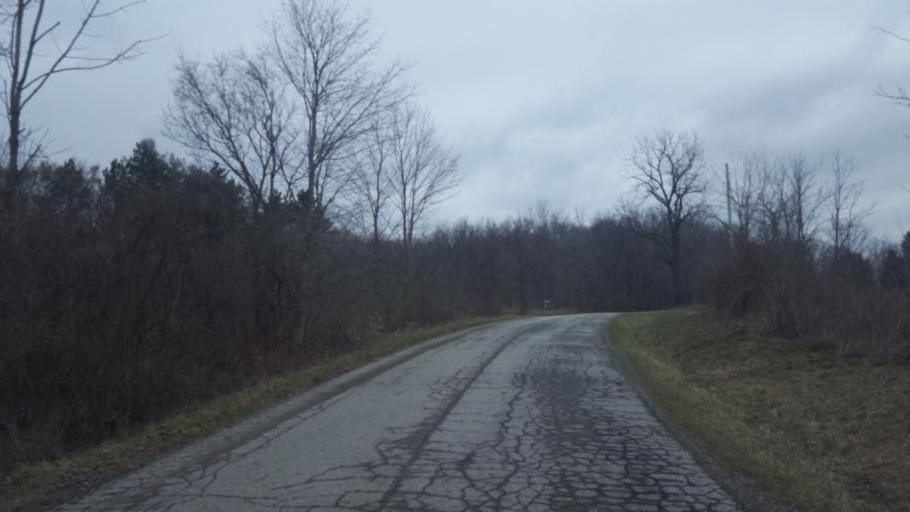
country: US
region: Ohio
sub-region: Delaware County
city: Ashley
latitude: 40.4258
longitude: -83.0106
